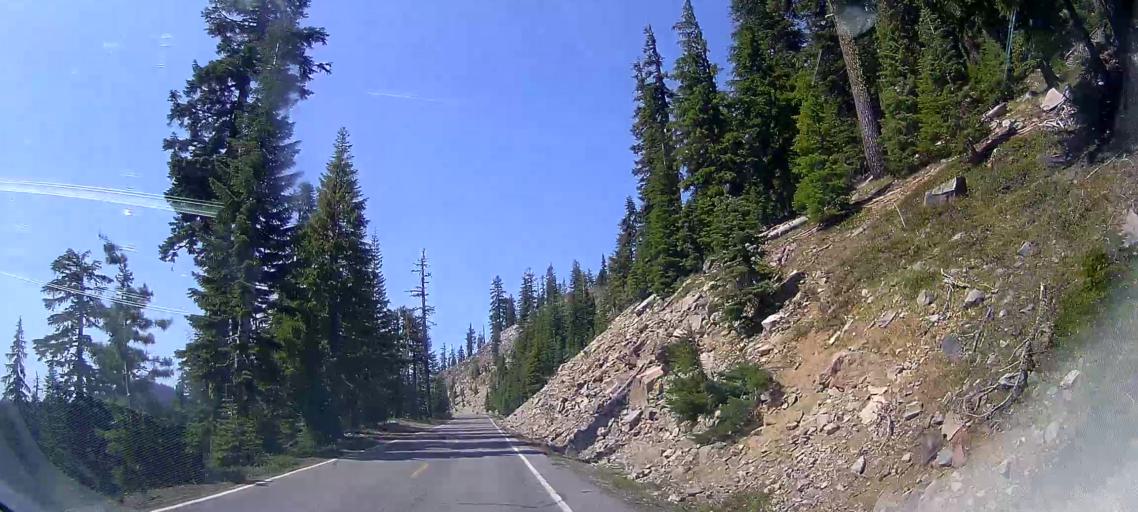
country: US
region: Oregon
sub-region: Klamath County
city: Klamath Falls
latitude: 42.8794
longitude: -122.1030
